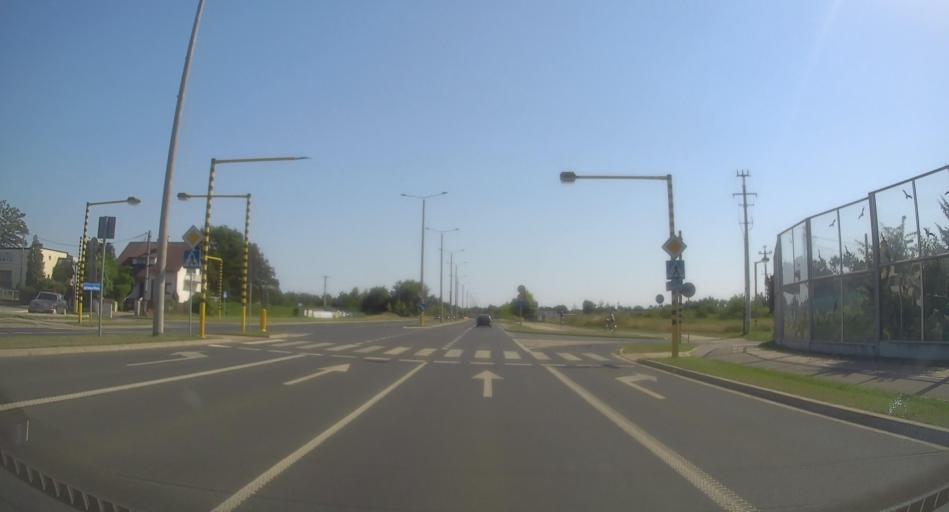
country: PL
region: Lodz Voivodeship
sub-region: Skierniewice
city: Skierniewice
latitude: 51.9483
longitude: 20.1589
